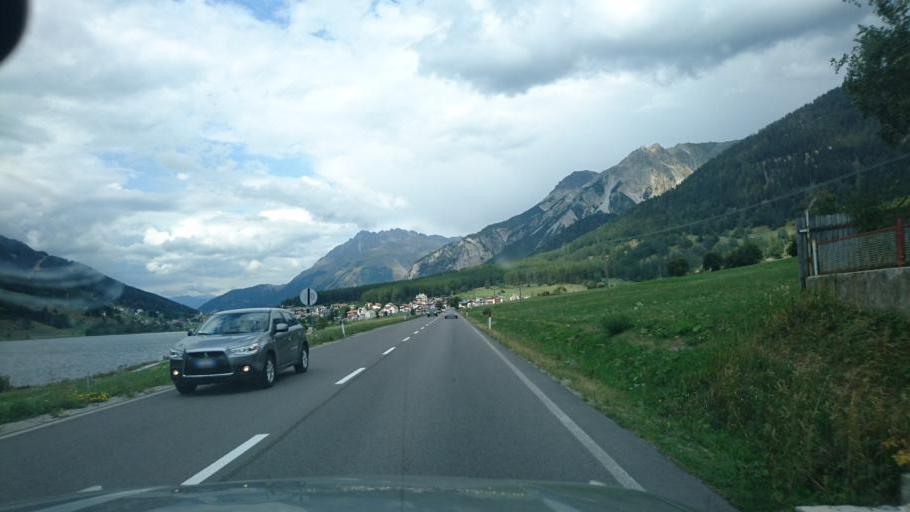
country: IT
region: Trentino-Alto Adige
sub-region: Bolzano
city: Curon Venosta
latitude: 46.7521
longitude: 10.5360
